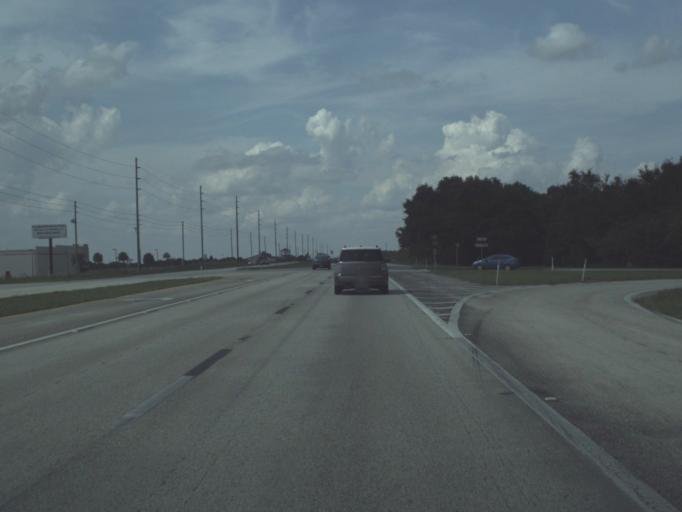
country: US
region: Florida
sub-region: Polk County
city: Lake Wales
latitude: 27.8713
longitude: -81.5935
